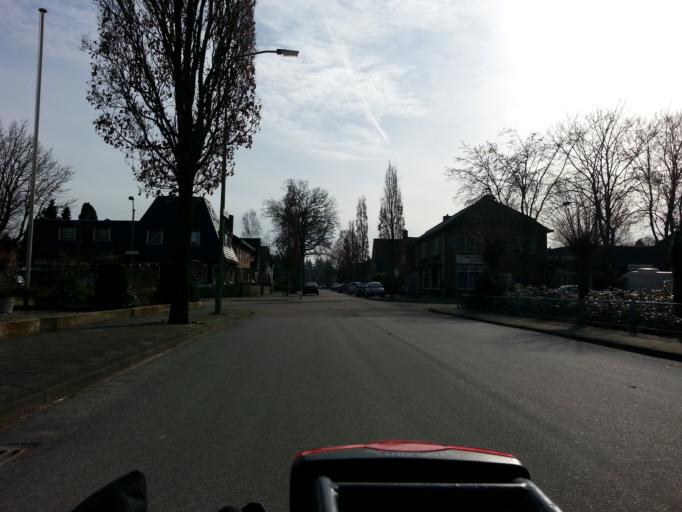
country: NL
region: Utrecht
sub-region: Gemeente Utrechtse Heuvelrug
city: Driebergen-Rijsenburg
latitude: 52.0795
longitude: 5.3124
